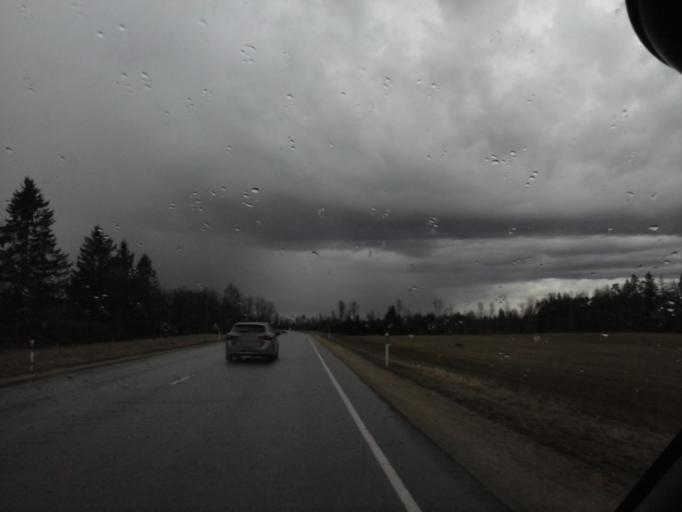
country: EE
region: Jogevamaa
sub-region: Poltsamaa linn
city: Poltsamaa
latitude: 58.6920
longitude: 25.9085
